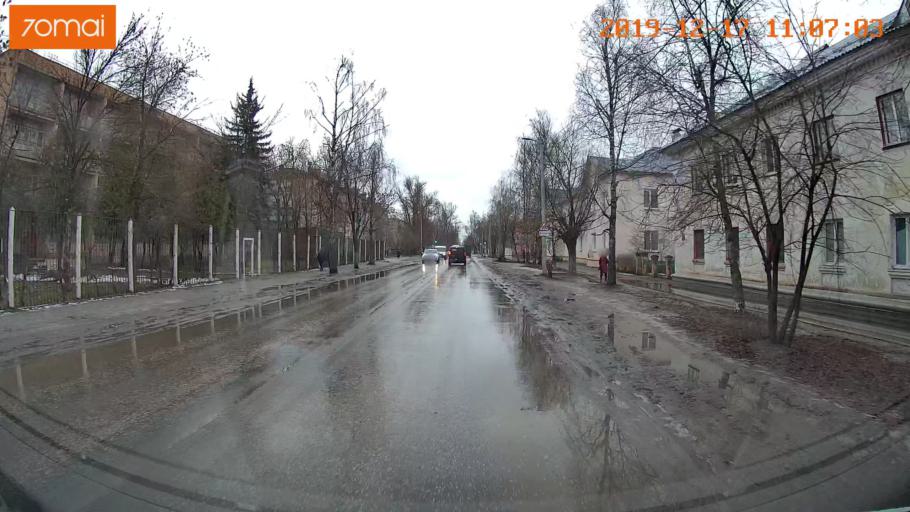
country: RU
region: Vladimir
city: Gus'-Khrustal'nyy
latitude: 55.6128
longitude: 40.6446
